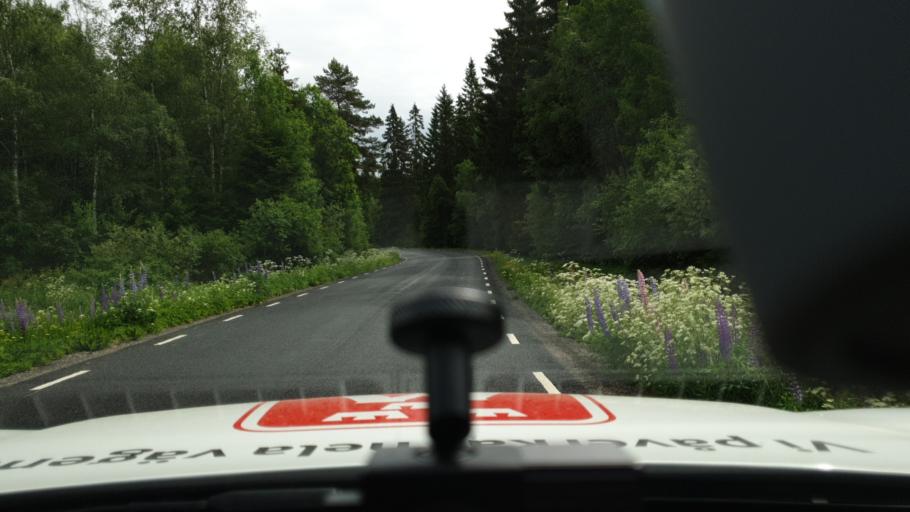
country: SE
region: Joenkoeping
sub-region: Mullsjo Kommun
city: Mullsjoe
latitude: 58.0047
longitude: 13.7228
